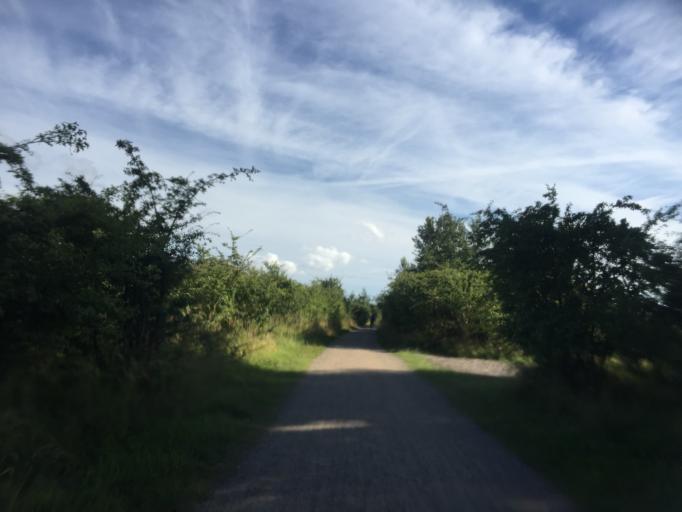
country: DK
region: Capital Region
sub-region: Kobenhavn
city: Christianshavn
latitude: 55.6504
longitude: 12.5826
